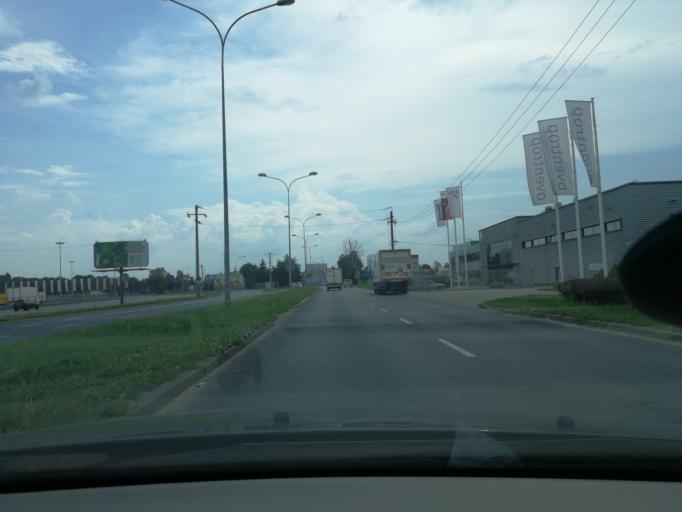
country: PL
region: Masovian Voivodeship
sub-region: Powiat pruszkowski
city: Piastow
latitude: 52.2170
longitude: 20.8387
